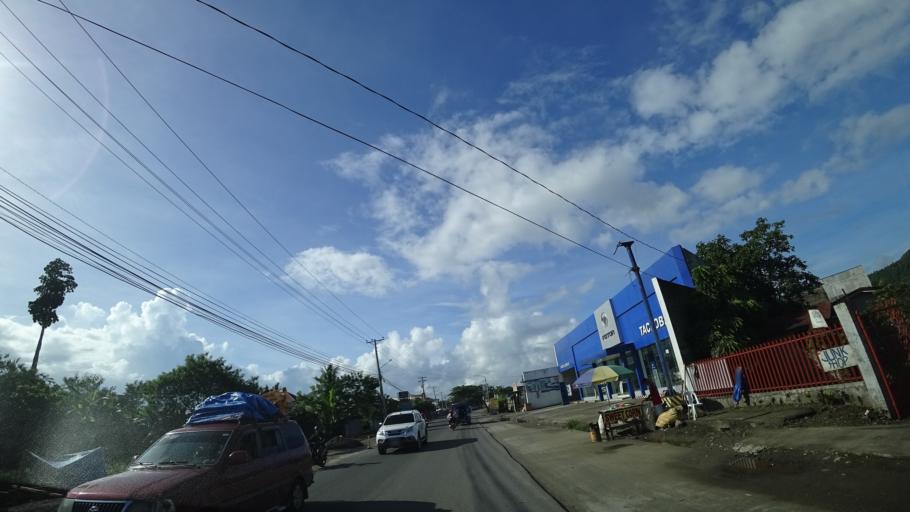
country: PH
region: Eastern Visayas
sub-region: Province of Leyte
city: Panalanoy
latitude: 11.2207
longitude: 124.9928
